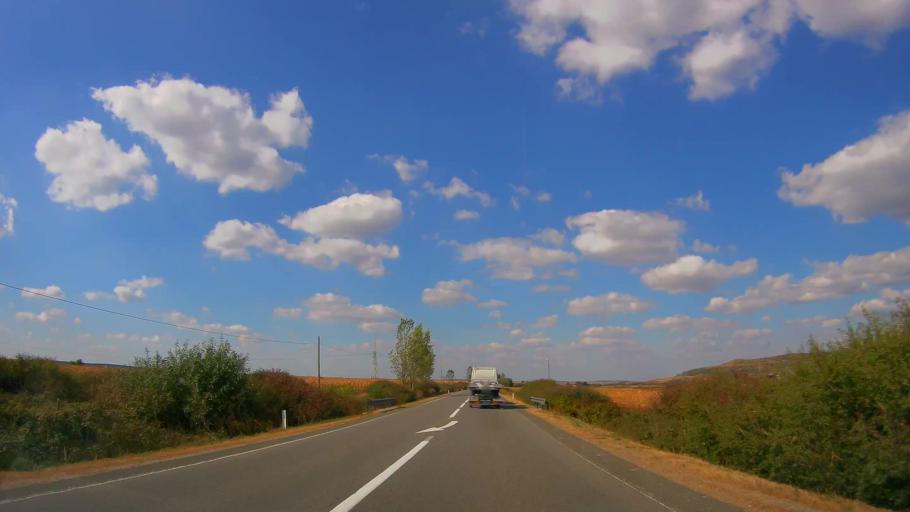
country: RO
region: Salaj
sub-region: Comuna Bobota
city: Dersida
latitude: 47.3673
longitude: 22.7907
